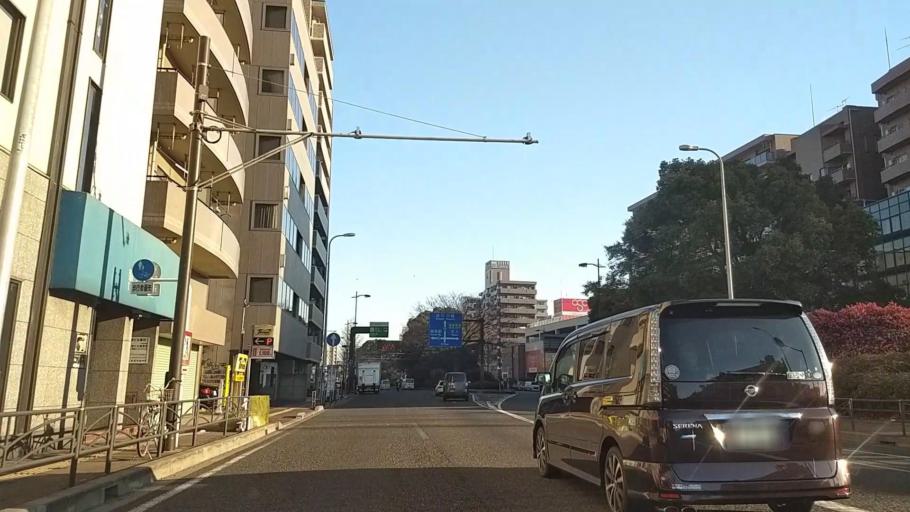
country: JP
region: Kanagawa
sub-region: Kawasaki-shi
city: Kawasaki
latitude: 35.5049
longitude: 139.6785
